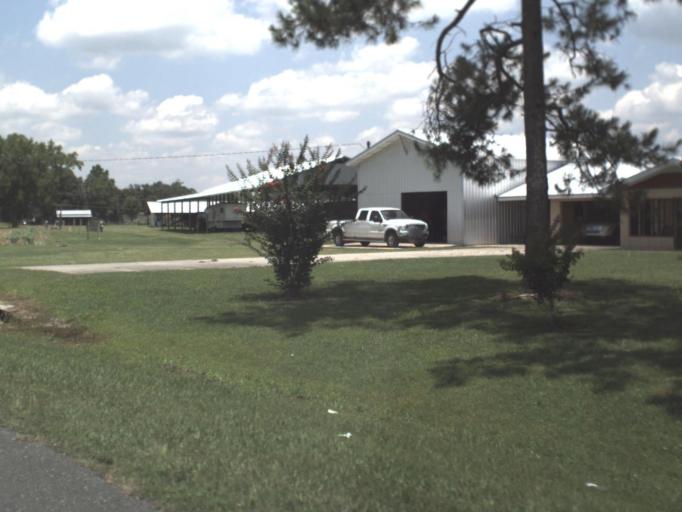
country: US
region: Florida
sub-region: Bradford County
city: Starke
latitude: 30.0322
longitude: -82.1604
